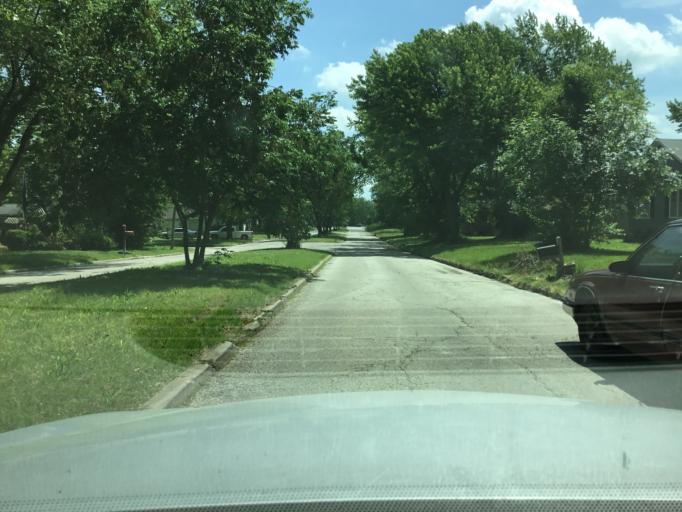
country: US
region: Kansas
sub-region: Labette County
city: Parsons
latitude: 37.3478
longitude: -95.2622
